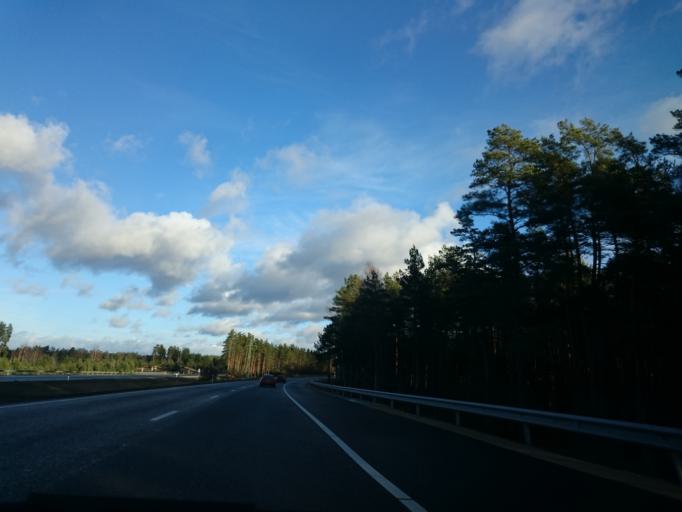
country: LV
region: Garkalne
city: Garkalne
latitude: 57.0574
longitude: 24.4561
